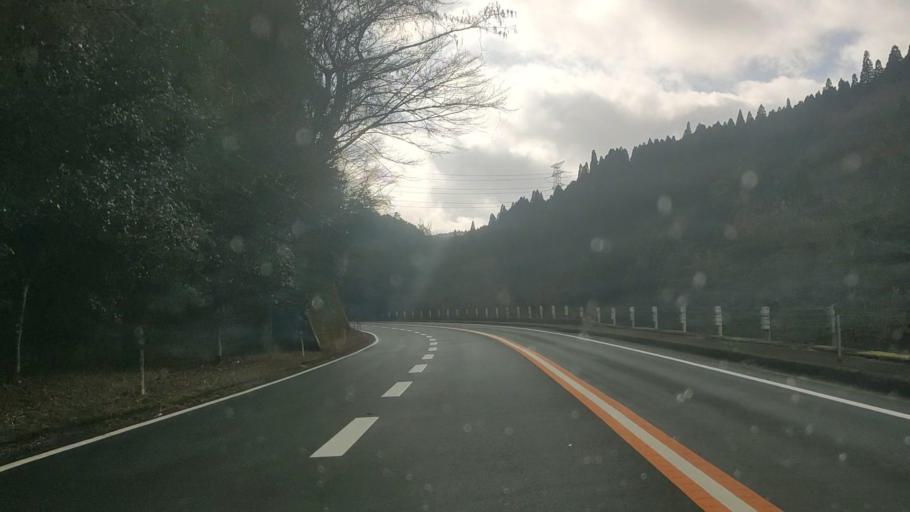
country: JP
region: Kumamoto
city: Hitoyoshi
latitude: 32.1133
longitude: 130.8056
